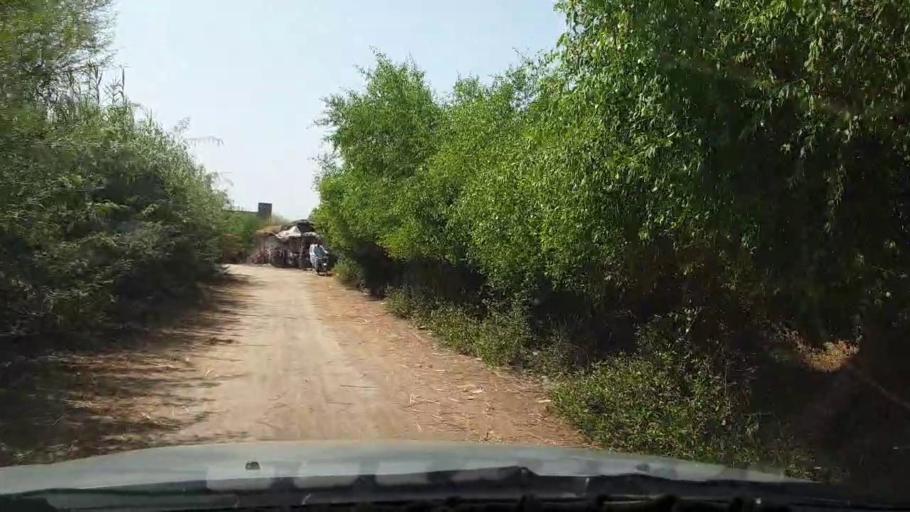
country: PK
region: Sindh
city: Tando Muhammad Khan
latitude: 25.1208
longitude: 68.6200
